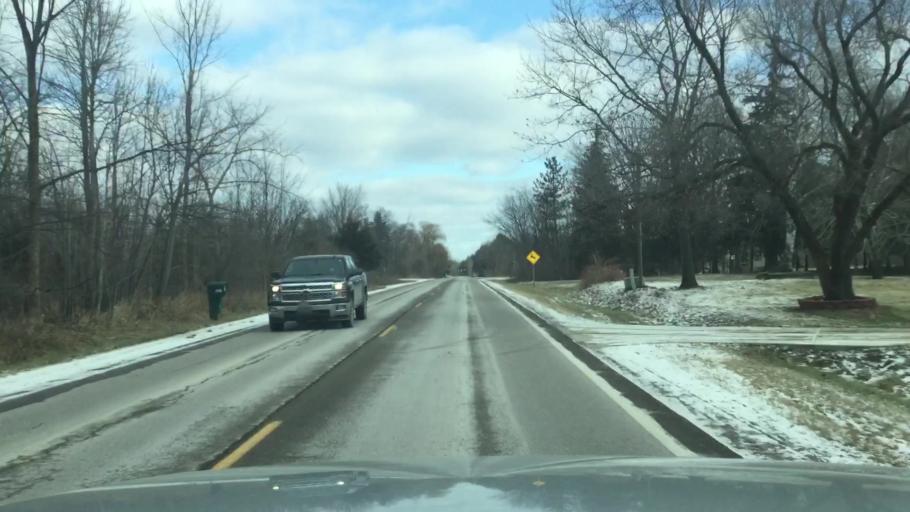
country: US
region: Michigan
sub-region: Genesee County
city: Linden
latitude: 42.8584
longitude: -83.7750
